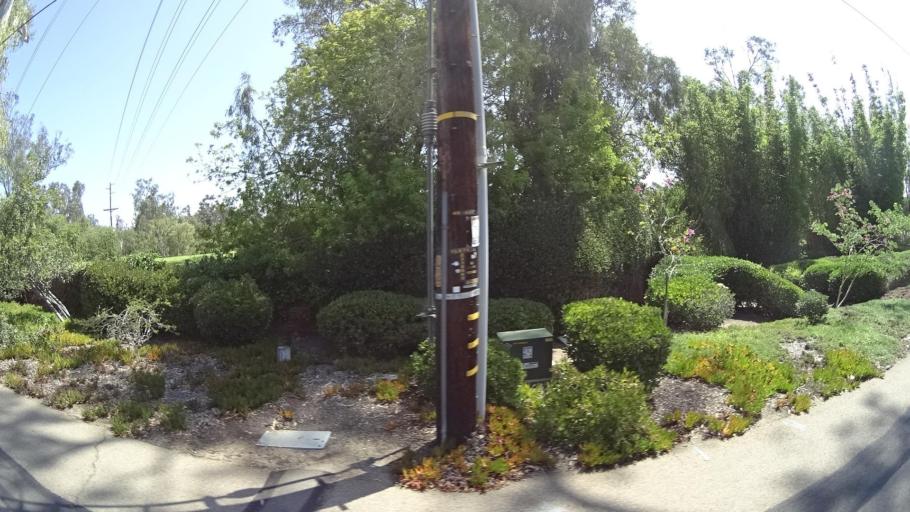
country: US
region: California
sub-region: San Diego County
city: Rancho Santa Fe
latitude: 32.9977
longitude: -117.2217
